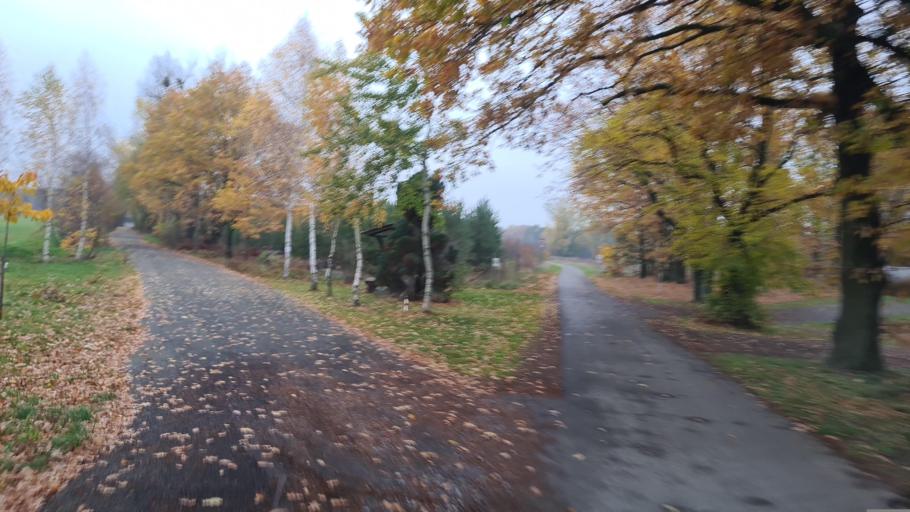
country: DE
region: Brandenburg
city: Kroppen
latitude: 51.3867
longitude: 13.8067
